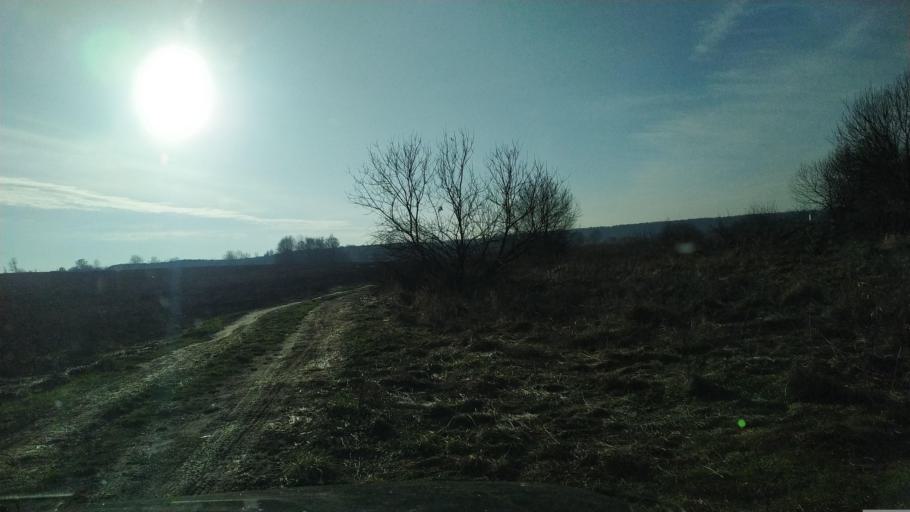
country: BY
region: Brest
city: Kamyanyets
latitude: 52.3788
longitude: 23.7778
